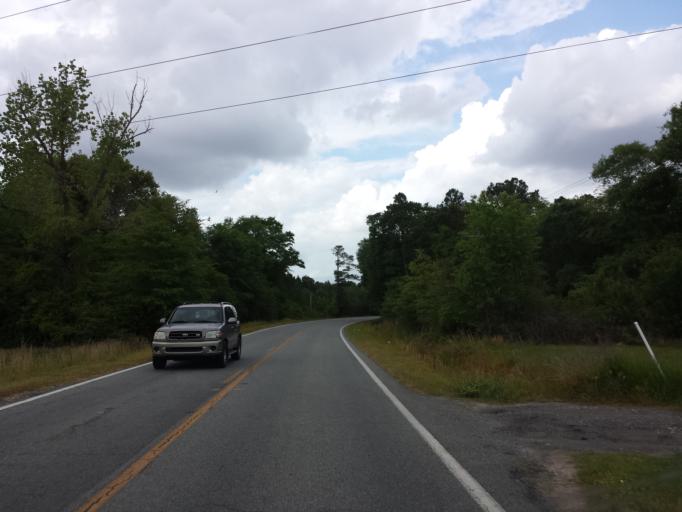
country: US
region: Georgia
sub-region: Cook County
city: Adel
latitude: 31.1079
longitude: -83.4135
